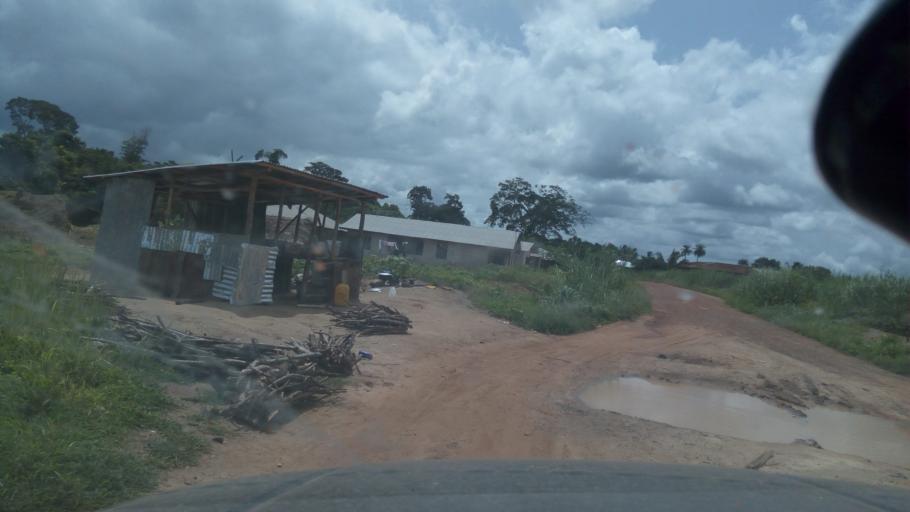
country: SL
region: Eastern Province
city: Kenema
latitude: 7.8781
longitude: -11.1595
